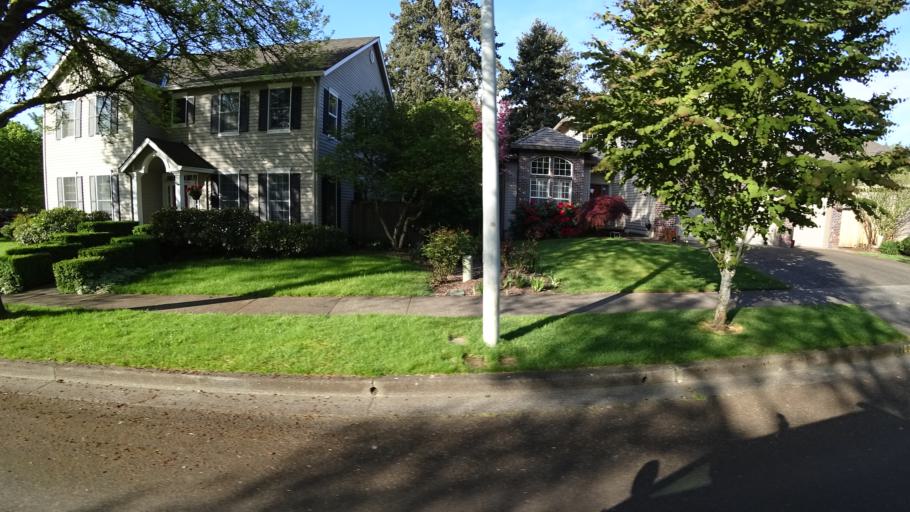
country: US
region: Oregon
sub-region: Washington County
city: King City
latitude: 45.4433
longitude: -122.8172
